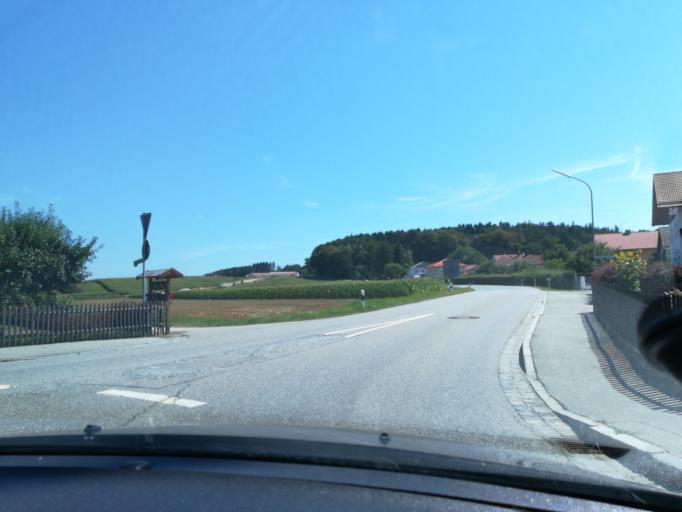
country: DE
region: Bavaria
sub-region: Upper Bavaria
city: Albaching
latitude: 48.1092
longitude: 12.1156
